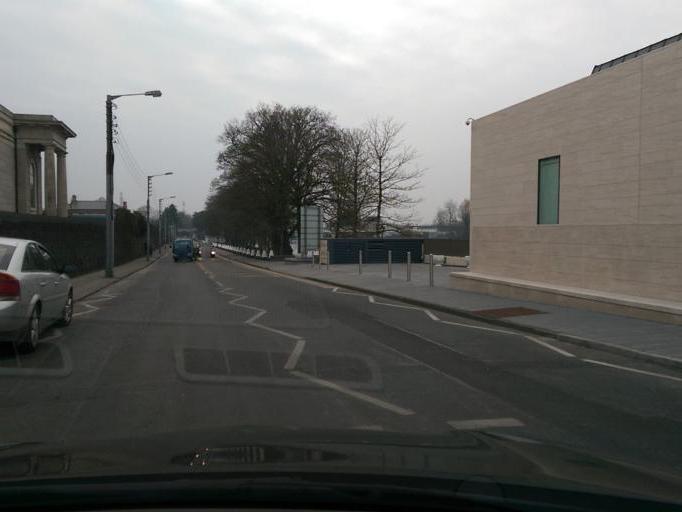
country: IE
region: Leinster
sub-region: An Iarmhi
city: Athlone
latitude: 53.4238
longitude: -7.9431
